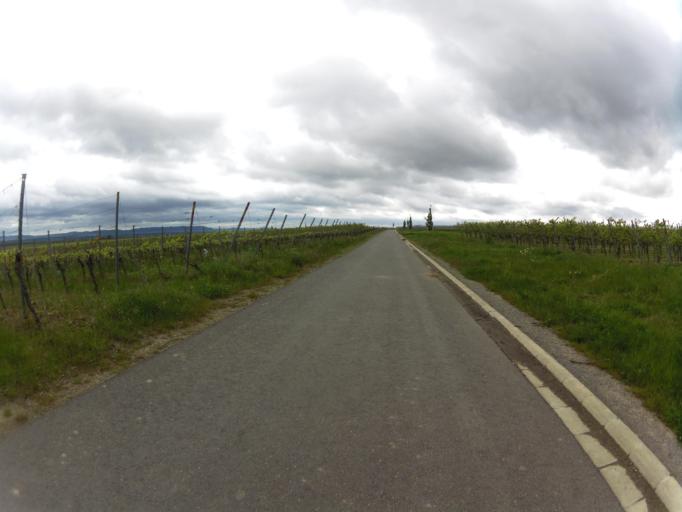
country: DE
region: Bavaria
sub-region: Regierungsbezirk Unterfranken
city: Sommerach
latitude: 49.8426
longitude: 10.2056
